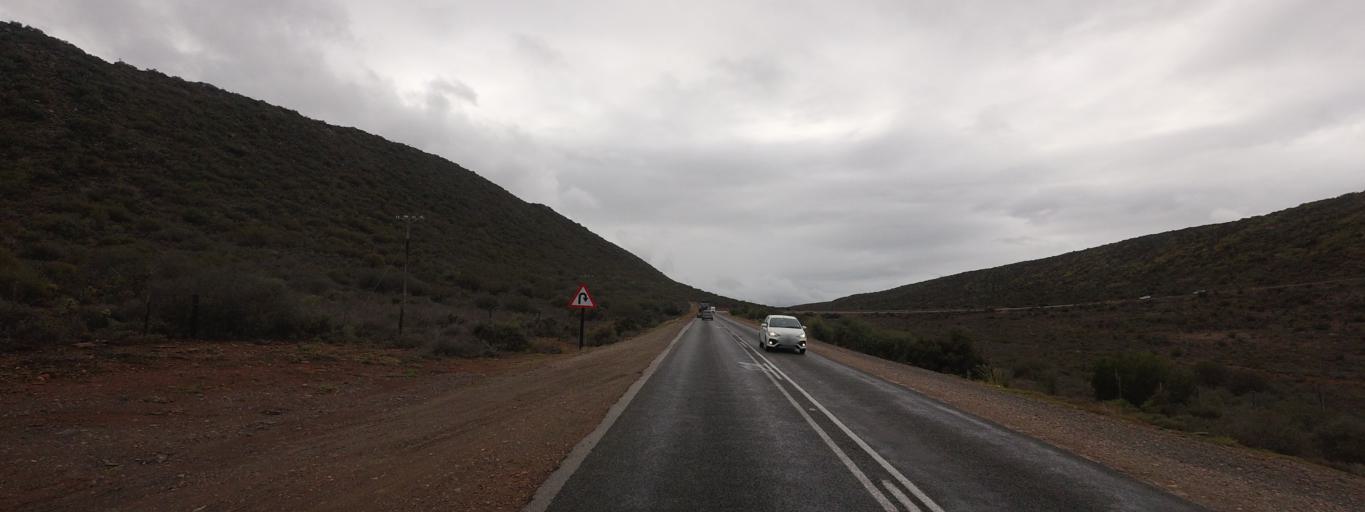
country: ZA
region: Western Cape
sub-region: Eden District Municipality
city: Oudtshoorn
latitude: -33.6840
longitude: 22.2707
